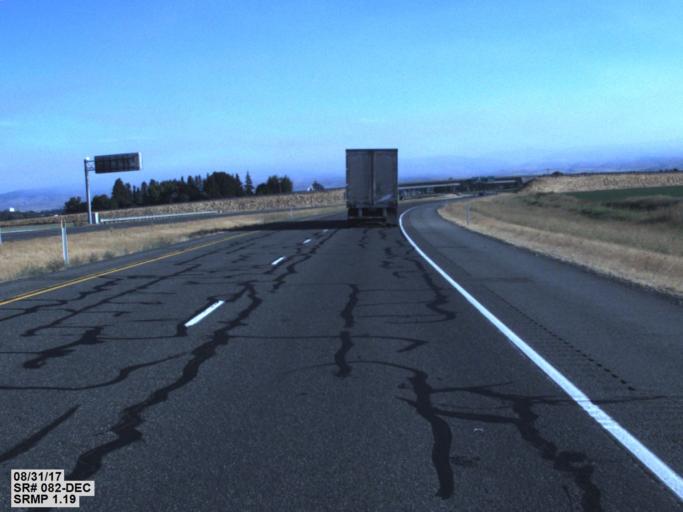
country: US
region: Washington
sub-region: Kittitas County
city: Ellensburg
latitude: 46.9543
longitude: -120.5075
